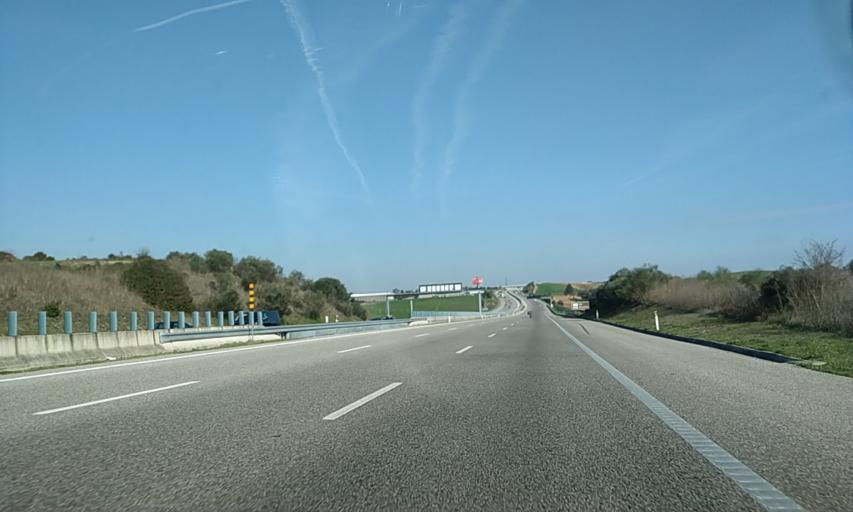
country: PT
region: Santarem
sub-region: Alcanena
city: Alcanena
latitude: 39.3508
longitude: -8.6460
